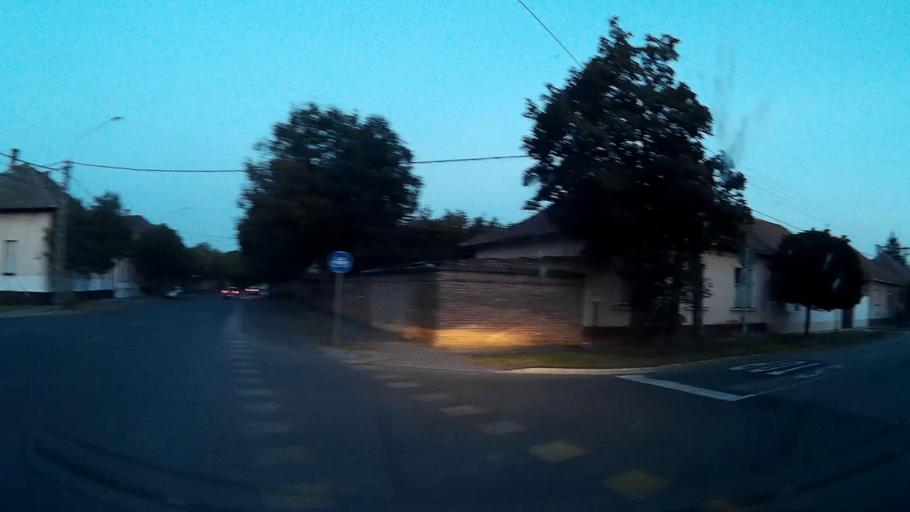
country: HU
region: Pest
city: Cegled
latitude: 47.1743
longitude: 19.7899
